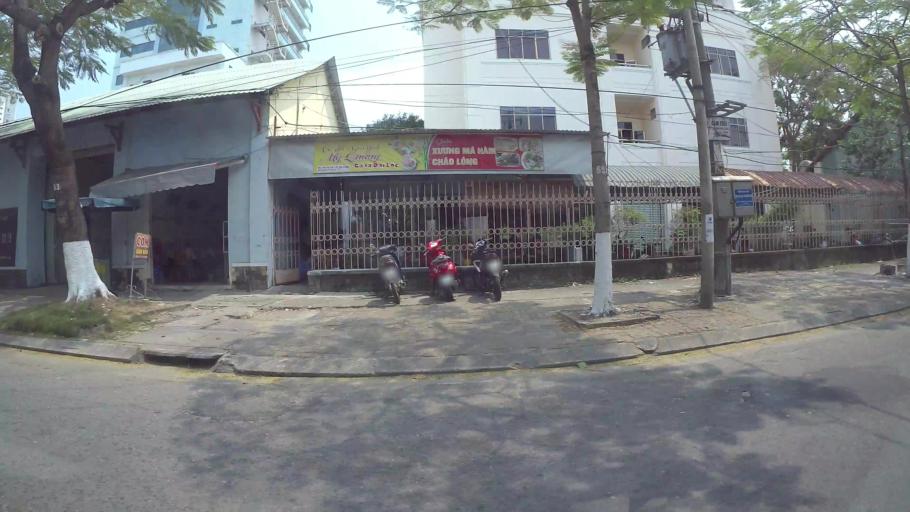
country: VN
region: Da Nang
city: Da Nang
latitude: 16.0780
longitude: 108.2195
